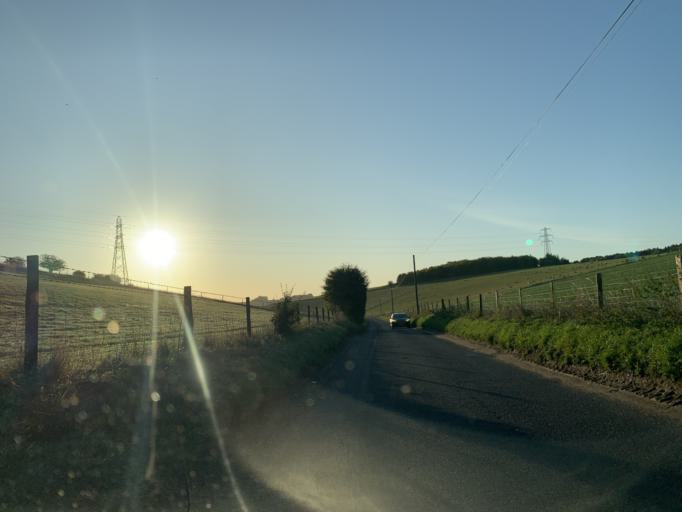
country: GB
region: England
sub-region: Wiltshire
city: Woodford
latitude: 51.1253
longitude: -1.8411
